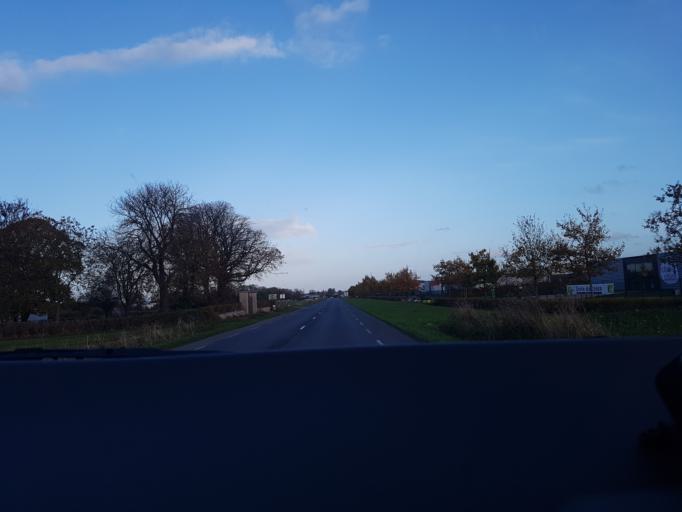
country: FR
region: Lower Normandy
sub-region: Departement du Calvados
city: Demouville
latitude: 49.1729
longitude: -0.2731
